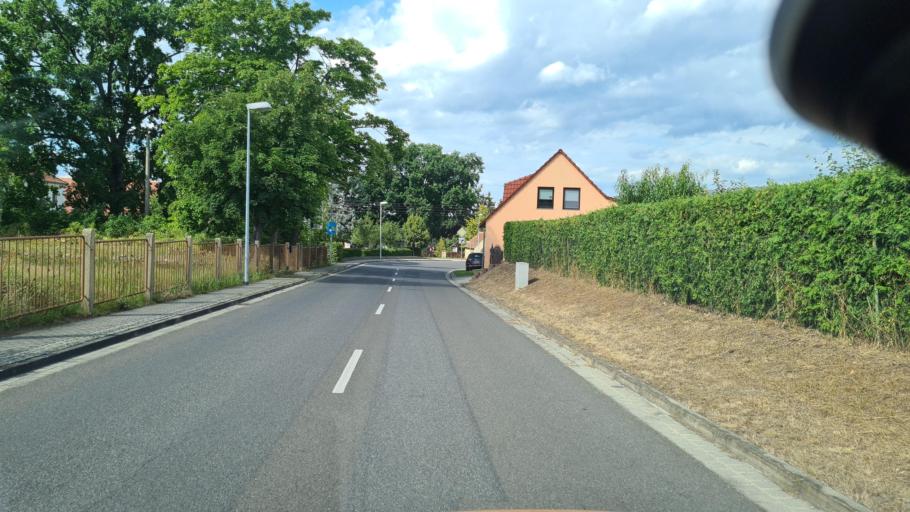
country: DE
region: Brandenburg
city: Neupetershain
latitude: 51.6249
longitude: 14.1614
